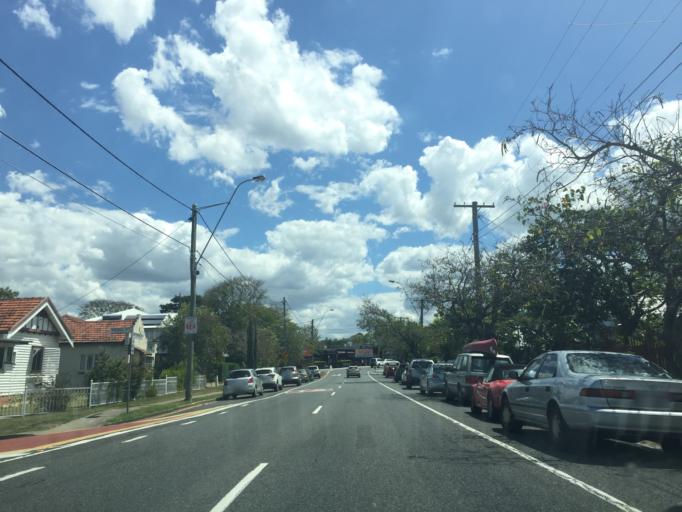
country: AU
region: Queensland
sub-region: Brisbane
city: Milton
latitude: -27.4484
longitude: 152.9794
